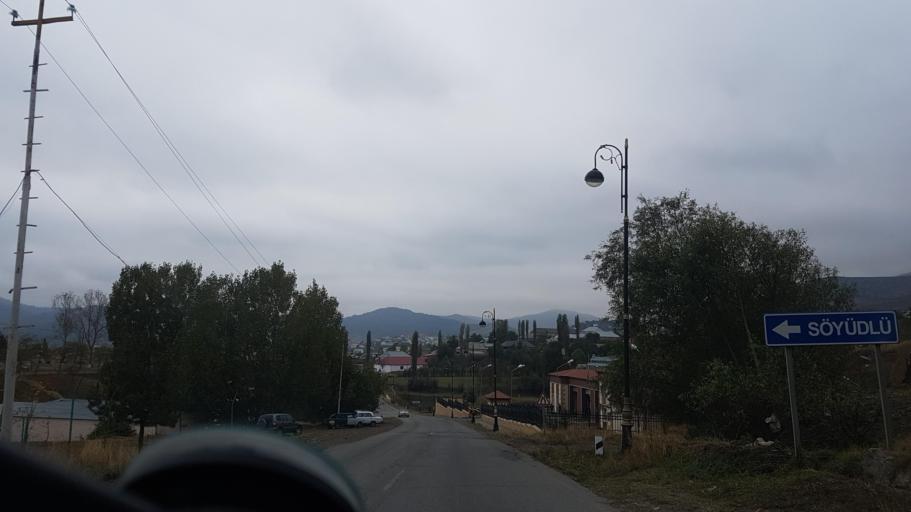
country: AZ
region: Gadabay Rayon
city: Ariqdam
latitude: 40.5967
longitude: 45.8106
